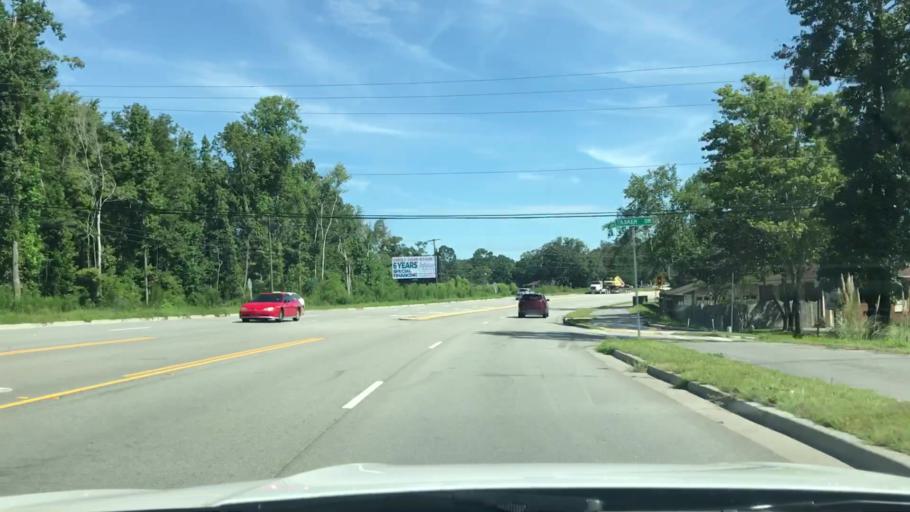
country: US
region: South Carolina
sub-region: Dorchester County
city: Centerville
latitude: 32.9651
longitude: -80.2023
